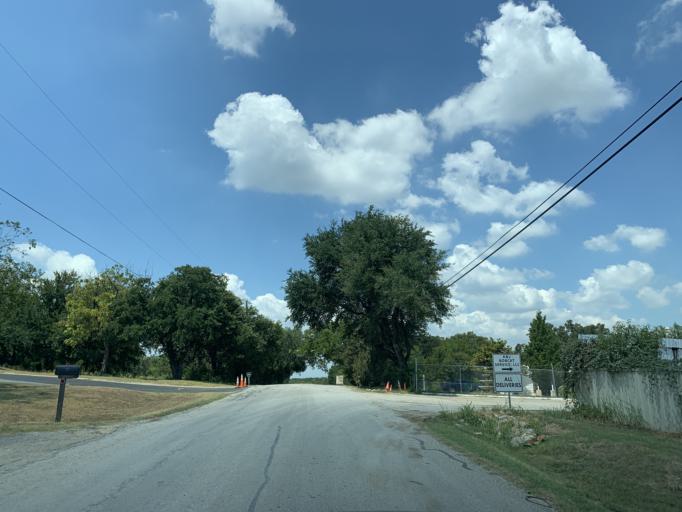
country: US
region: Texas
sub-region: Tarrant County
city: Lakeside
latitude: 32.8417
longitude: -97.5000
